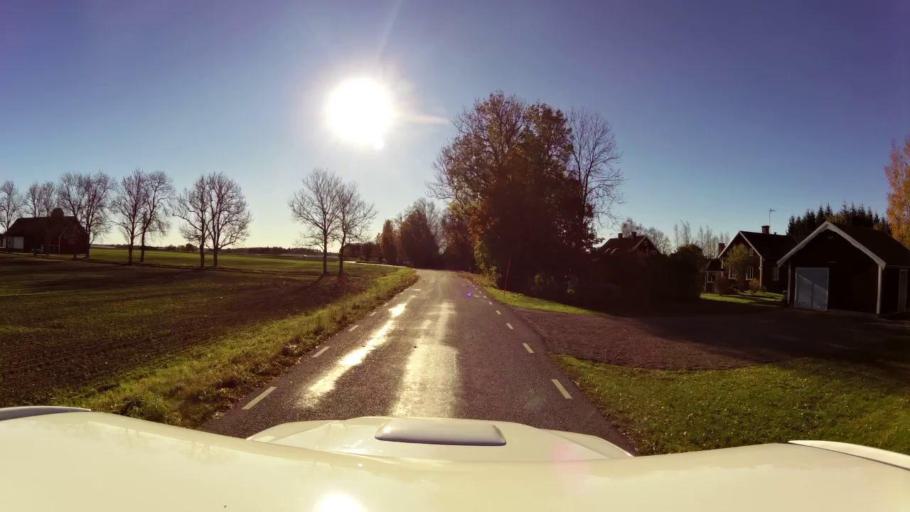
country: SE
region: OEstergoetland
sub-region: Linkopings Kommun
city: Ljungsbro
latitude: 58.4847
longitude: 15.4183
